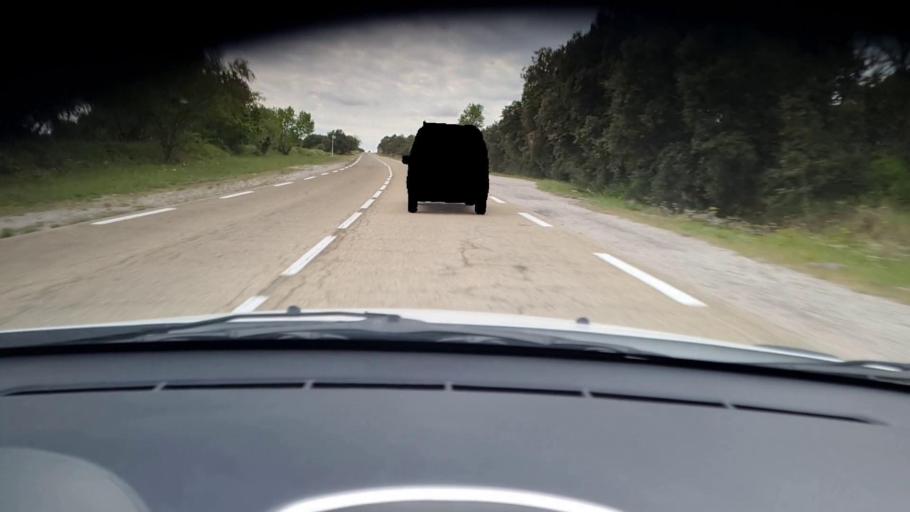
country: FR
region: Languedoc-Roussillon
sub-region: Departement du Gard
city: Poulx
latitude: 43.9131
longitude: 4.3879
